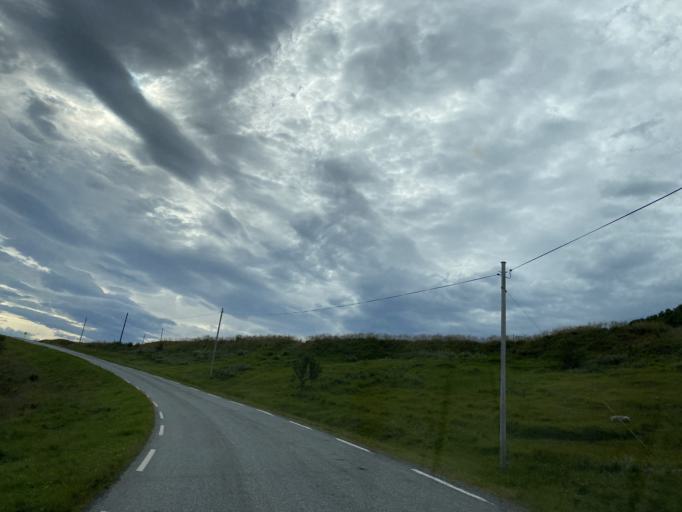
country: NO
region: Troms
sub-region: Karlsoy
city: Hansnes
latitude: 70.0942
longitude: 20.0831
